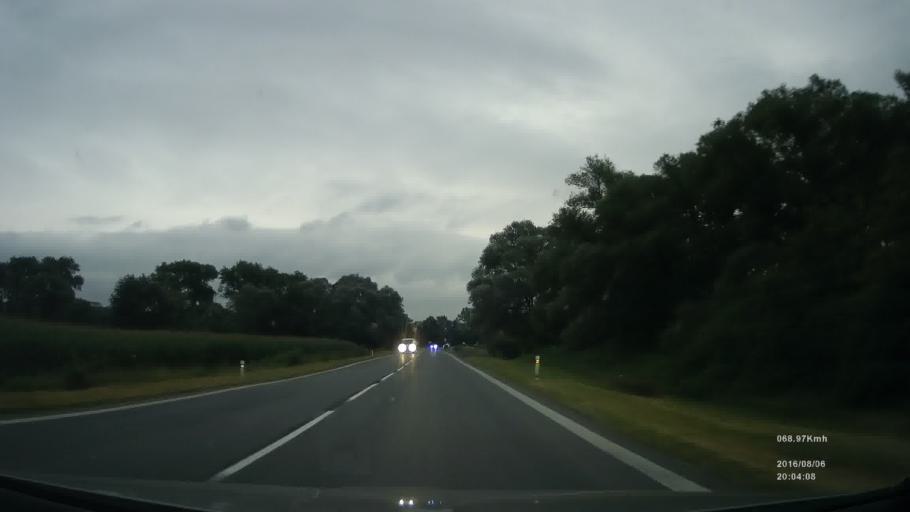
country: SK
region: Presovsky
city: Stropkov
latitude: 49.2437
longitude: 21.6184
